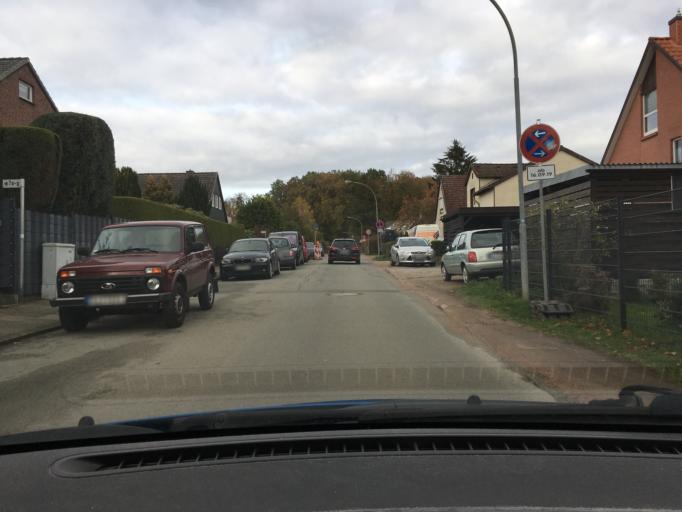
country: DE
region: Lower Saxony
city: Seevetal
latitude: 53.4114
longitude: 9.9889
